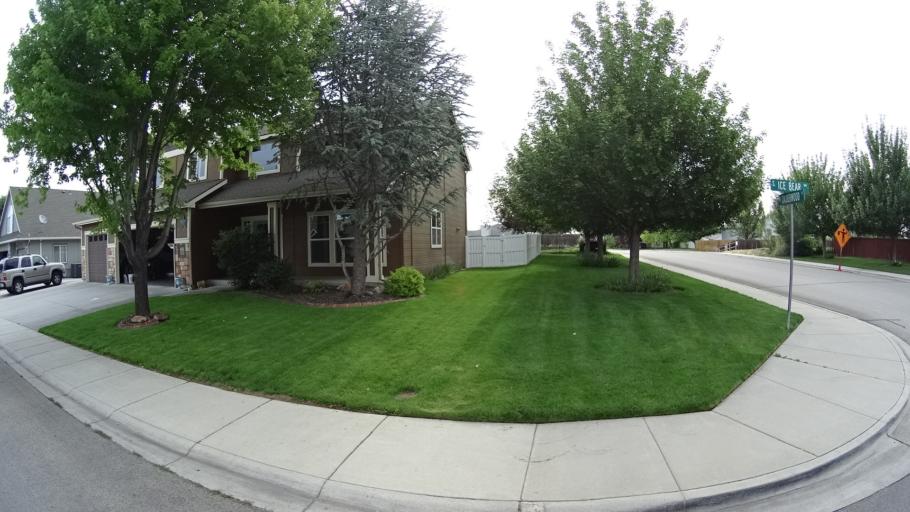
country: US
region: Idaho
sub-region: Ada County
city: Meridian
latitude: 43.5861
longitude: -116.3981
